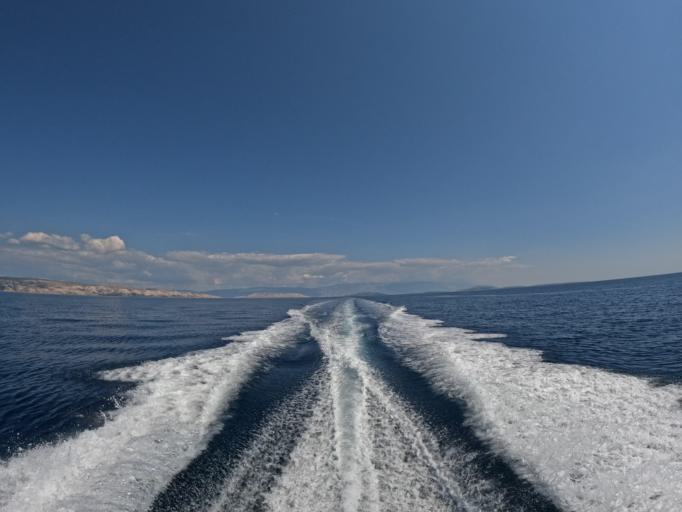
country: HR
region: Primorsko-Goranska
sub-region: Grad Krk
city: Krk
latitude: 44.9226
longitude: 14.5551
